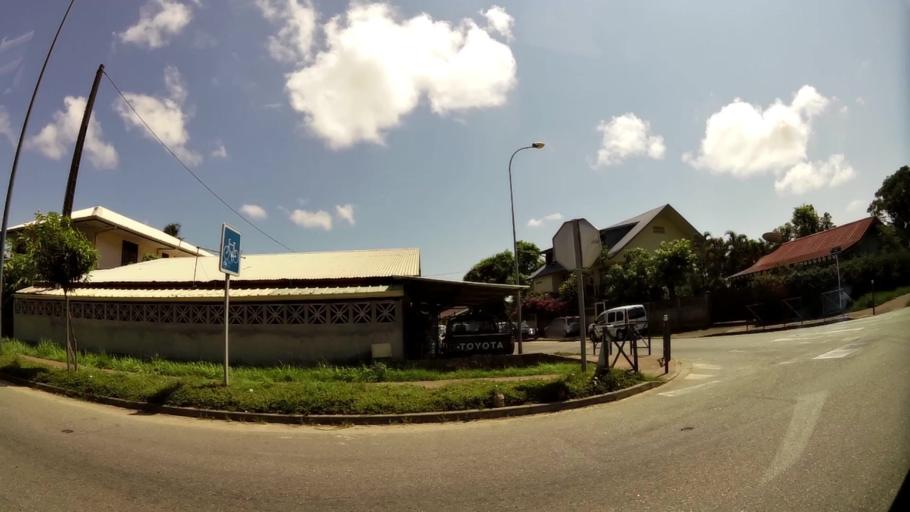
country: GF
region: Guyane
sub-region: Guyane
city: Cayenne
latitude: 4.9200
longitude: -52.3197
